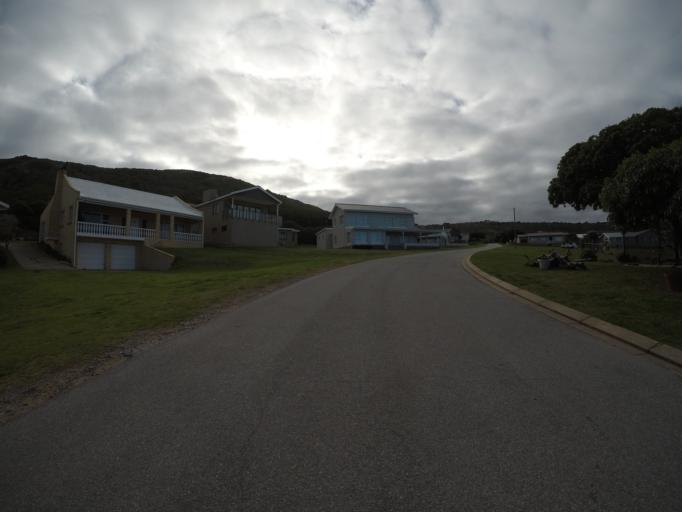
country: ZA
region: Western Cape
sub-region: Eden District Municipality
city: Riversdale
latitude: -34.4274
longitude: 21.3353
